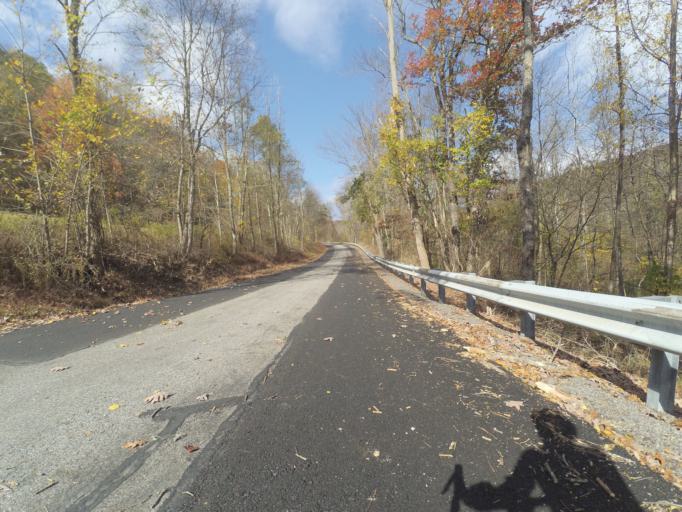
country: US
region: Pennsylvania
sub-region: Centre County
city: Stormstown
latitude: 40.8652
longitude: -77.9878
